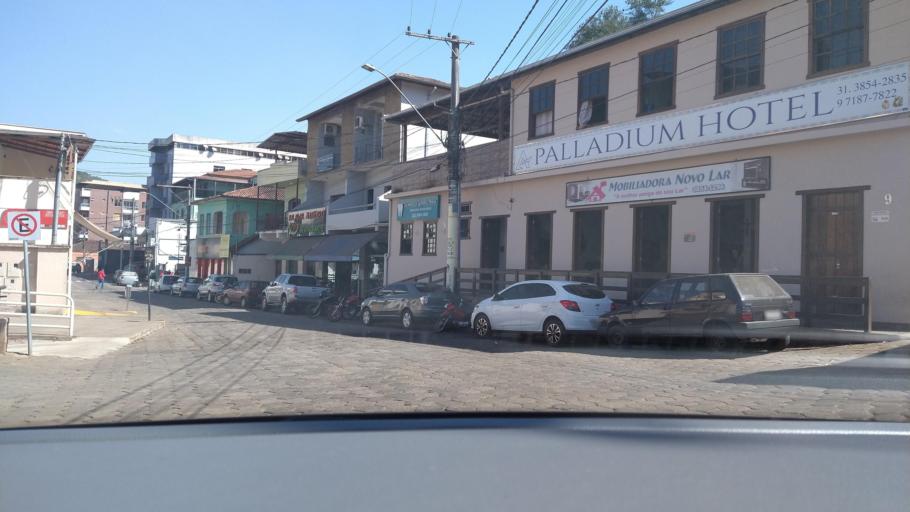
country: BR
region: Minas Gerais
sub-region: Rio Piracicaba
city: Rio Piracicaba
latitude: -19.9297
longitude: -43.1740
